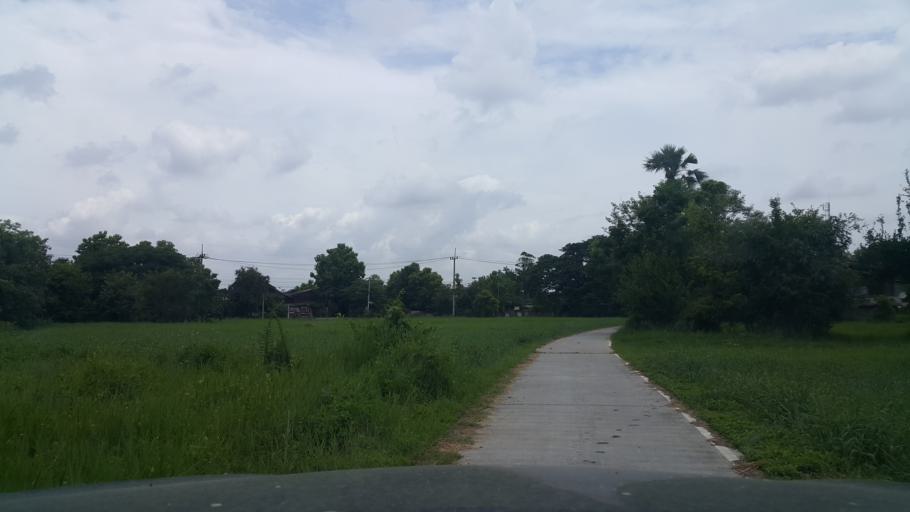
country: TH
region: Lamphun
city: Ban Thi
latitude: 18.6733
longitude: 99.1452
